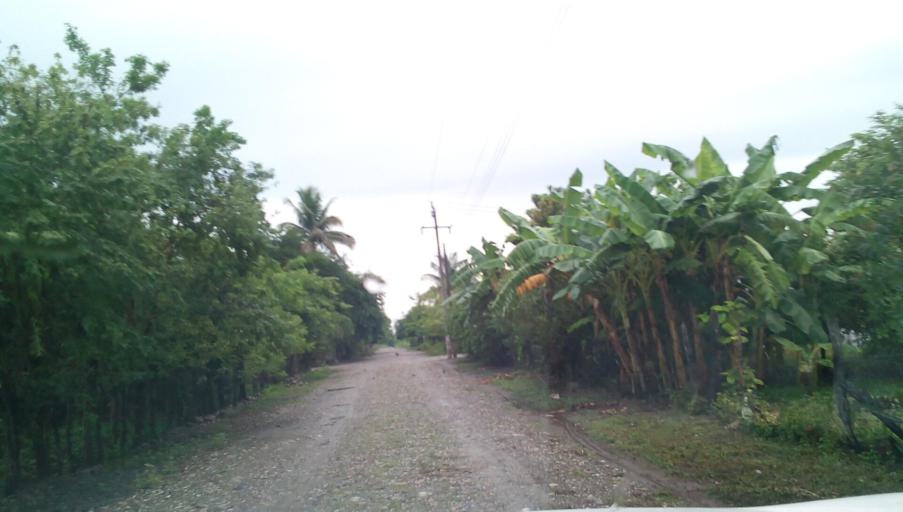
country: MX
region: Veracruz
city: Tempoal de Sanchez
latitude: 21.4177
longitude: -98.4302
